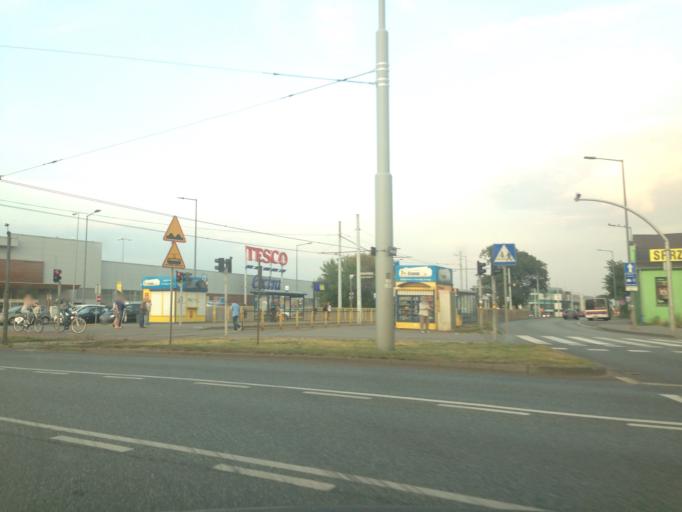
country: PL
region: Kujawsko-Pomorskie
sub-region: Bydgoszcz
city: Bydgoszcz
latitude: 53.1168
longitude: 18.0341
